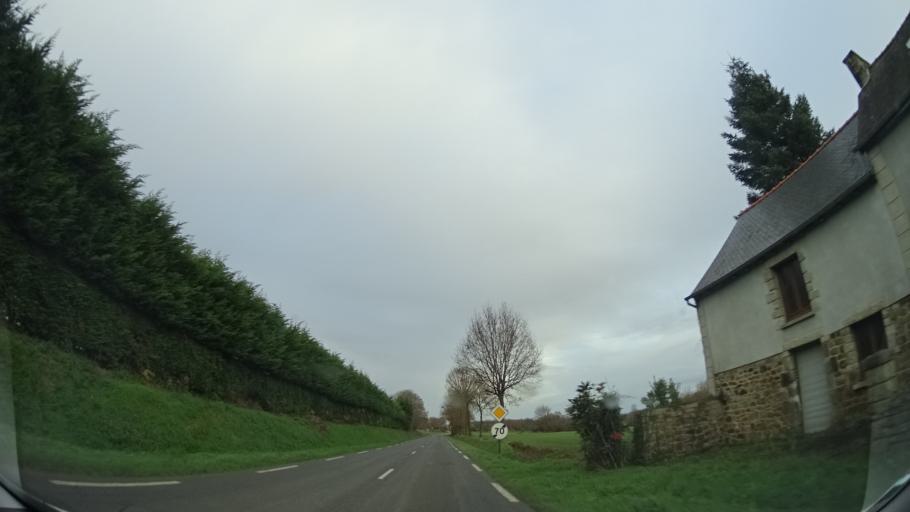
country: FR
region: Brittany
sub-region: Departement des Cotes-d'Armor
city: Evran
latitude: 48.3380
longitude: -1.9640
